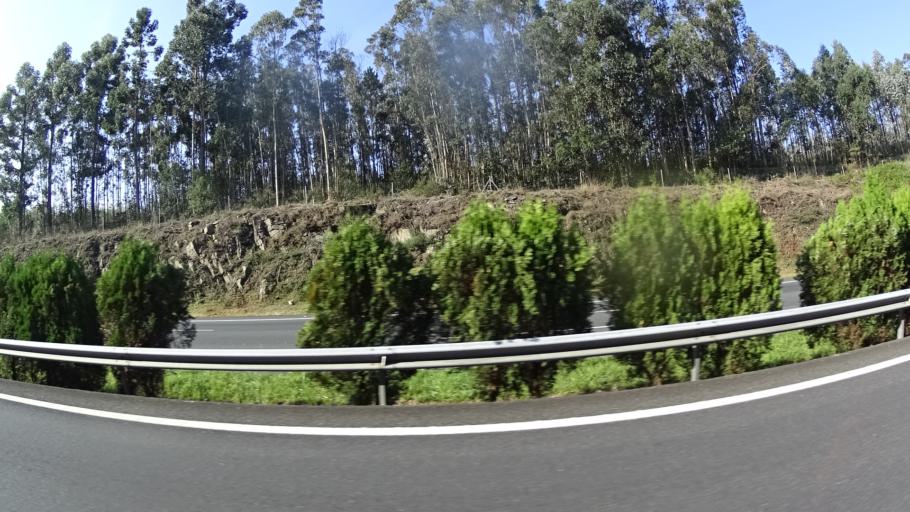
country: ES
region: Galicia
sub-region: Provincia da Coruna
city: Irixoa
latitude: 43.2378
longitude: -8.0902
